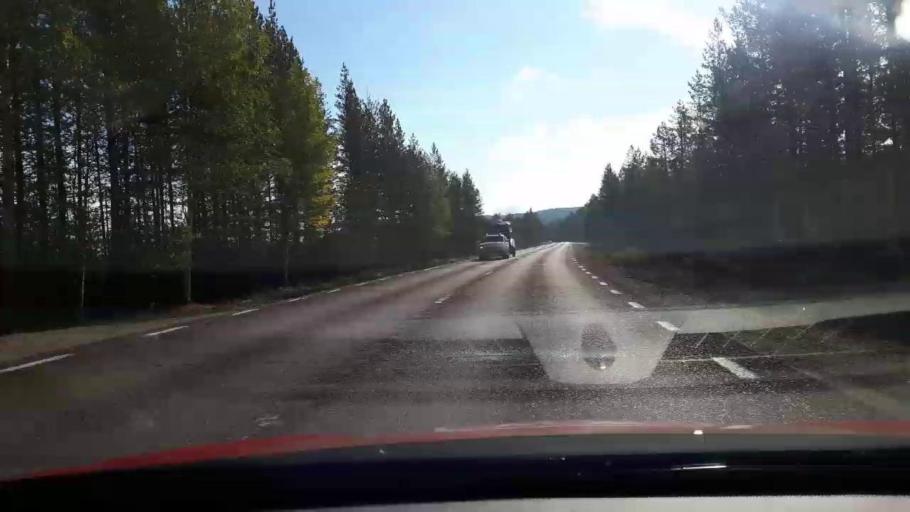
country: SE
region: Gaevleborg
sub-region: Ljusdals Kommun
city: Farila
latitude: 61.8985
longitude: 15.6505
